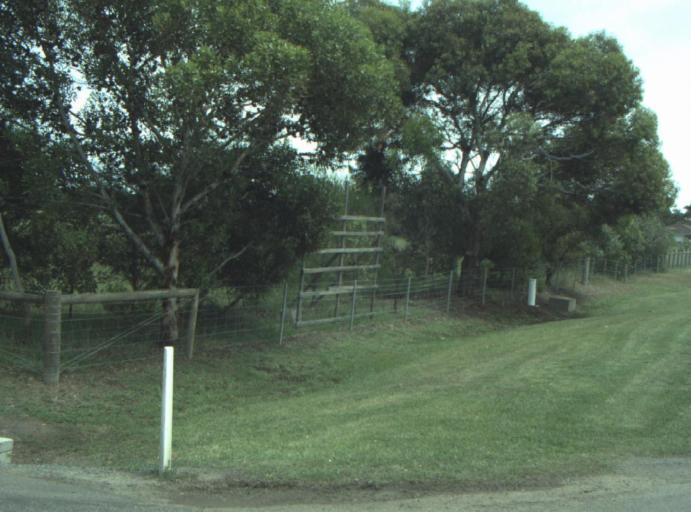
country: AU
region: Victoria
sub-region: Greater Geelong
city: Lara
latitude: -38.0216
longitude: 144.3842
